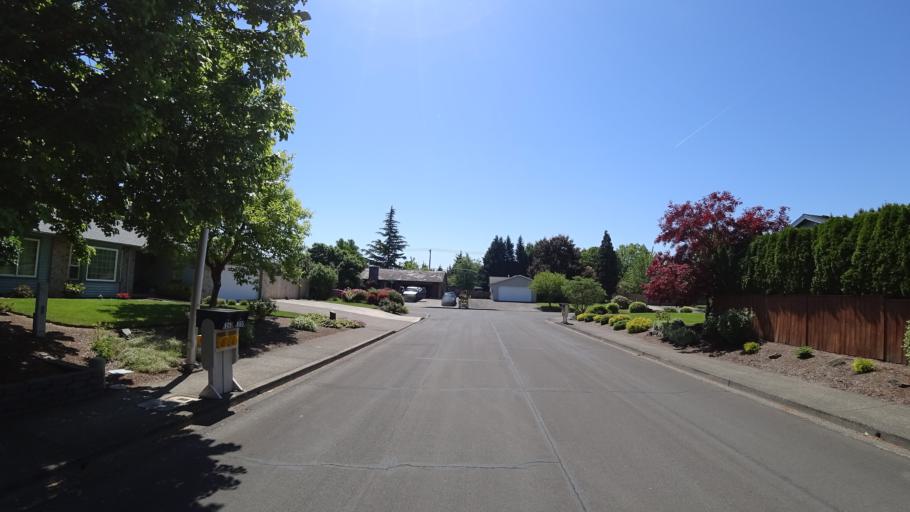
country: US
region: Oregon
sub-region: Washington County
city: Rockcreek
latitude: 45.5346
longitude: -122.9236
